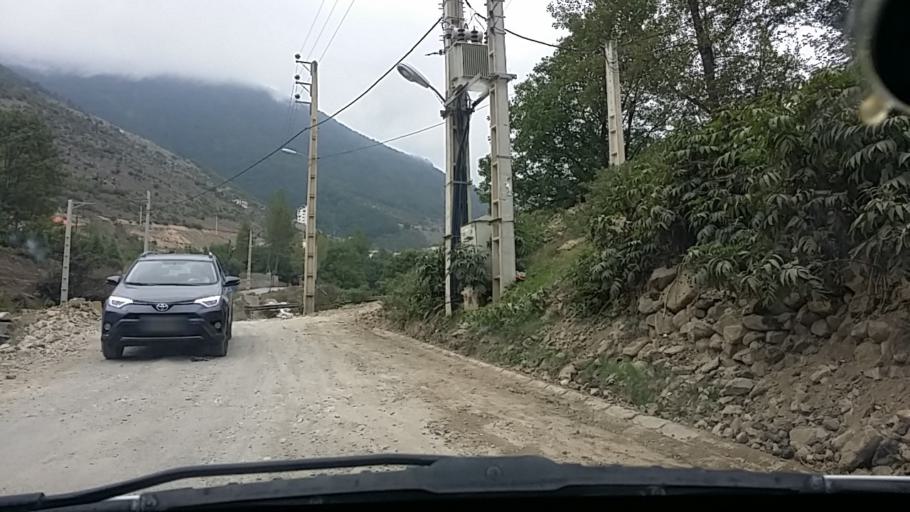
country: IR
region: Mazandaran
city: `Abbasabad
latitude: 36.4810
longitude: 51.1374
